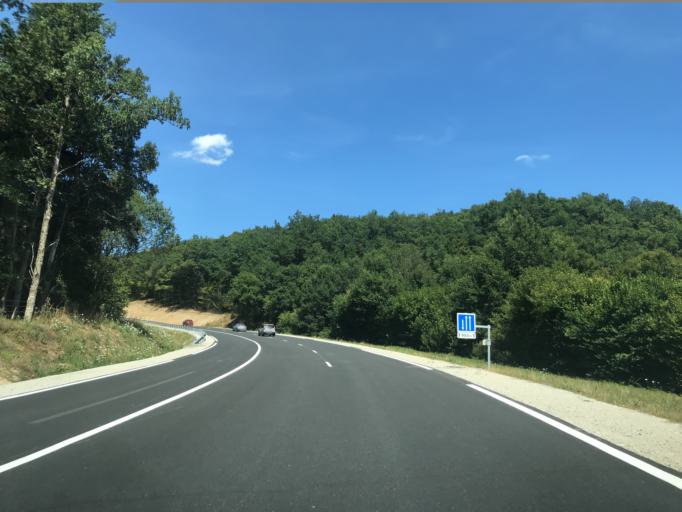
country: FR
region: Limousin
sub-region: Departement de la Creuse
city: Aubusson
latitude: 45.9314
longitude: 2.1929
